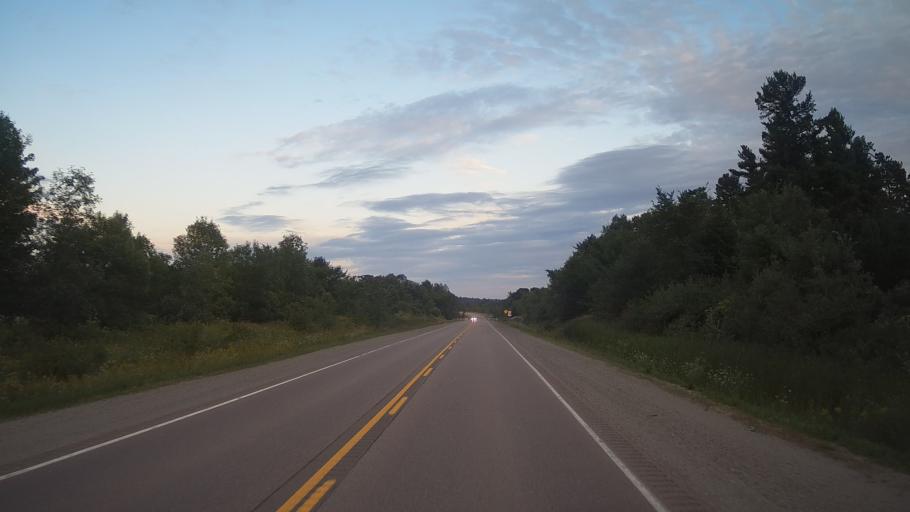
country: CA
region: Ontario
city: Pembroke
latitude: 45.7749
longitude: -77.0899
